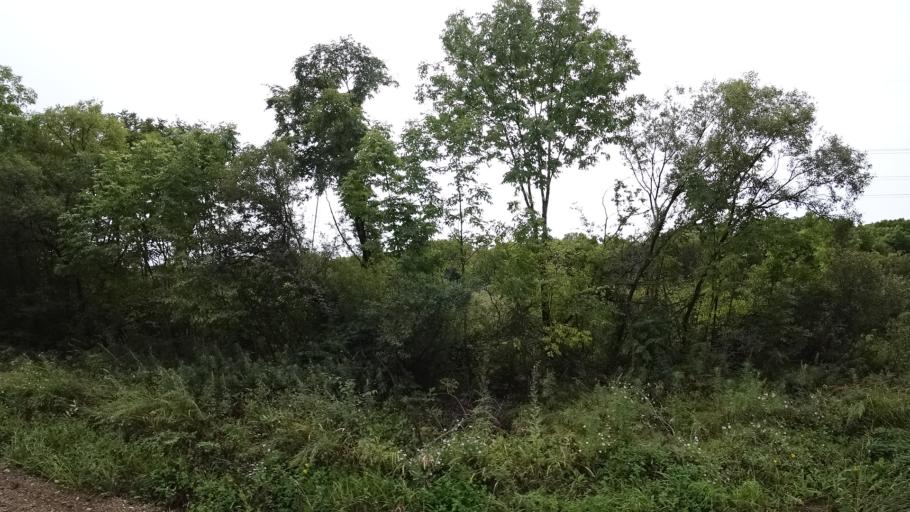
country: RU
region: Primorskiy
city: Lyalichi
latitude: 44.0783
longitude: 132.4540
